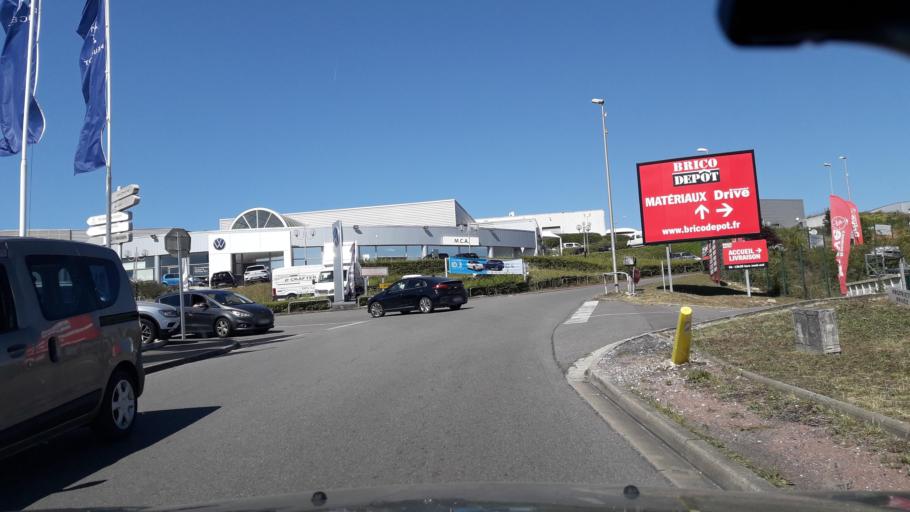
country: FR
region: Poitou-Charentes
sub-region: Departement de la Charente
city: Gond-Pontouvre
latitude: 45.6857
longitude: 0.1822
